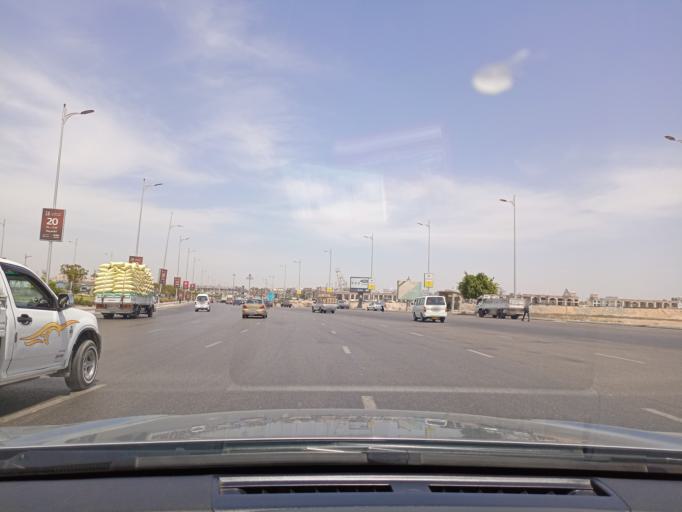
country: EG
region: Muhafazat al Qalyubiyah
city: Al Khankah
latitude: 30.1666
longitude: 31.4776
